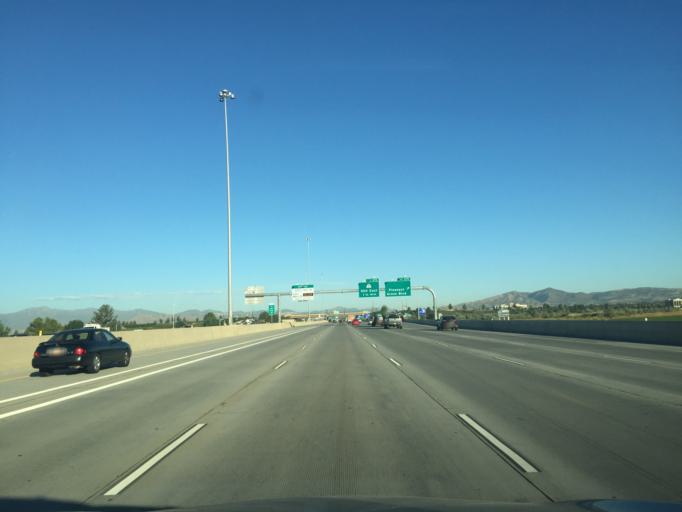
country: US
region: Utah
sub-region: Utah County
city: Pleasant Grove
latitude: 40.3465
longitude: -111.7633
